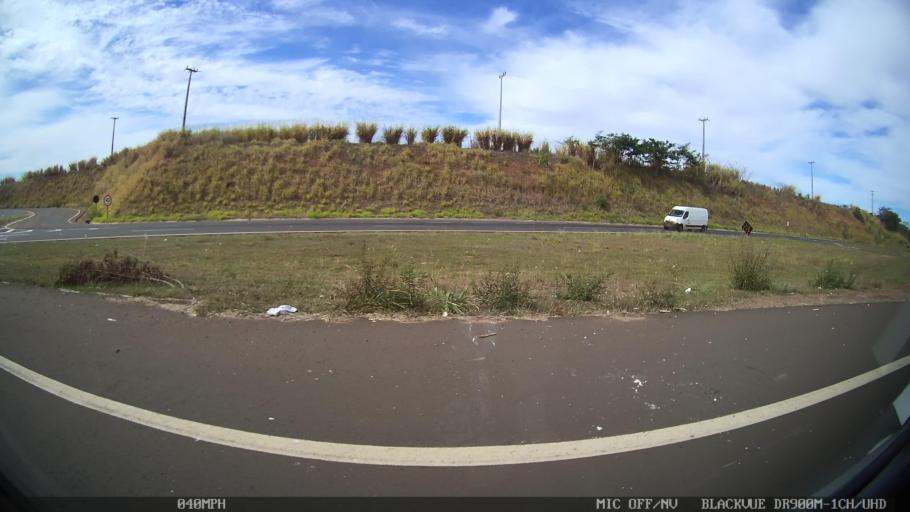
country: BR
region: Sao Paulo
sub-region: Catanduva
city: Catanduva
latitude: -21.1654
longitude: -48.9880
